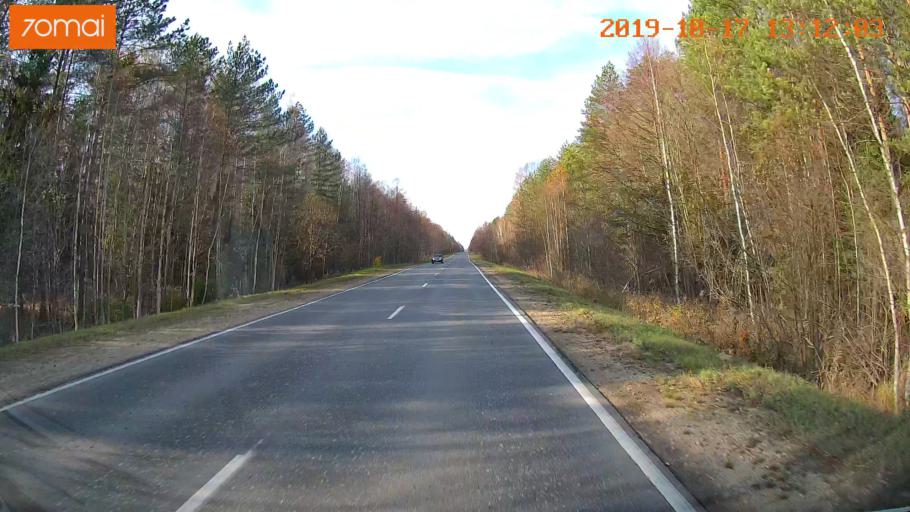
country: RU
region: Rjazan
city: Gus'-Zheleznyy
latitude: 55.0329
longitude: 41.2217
